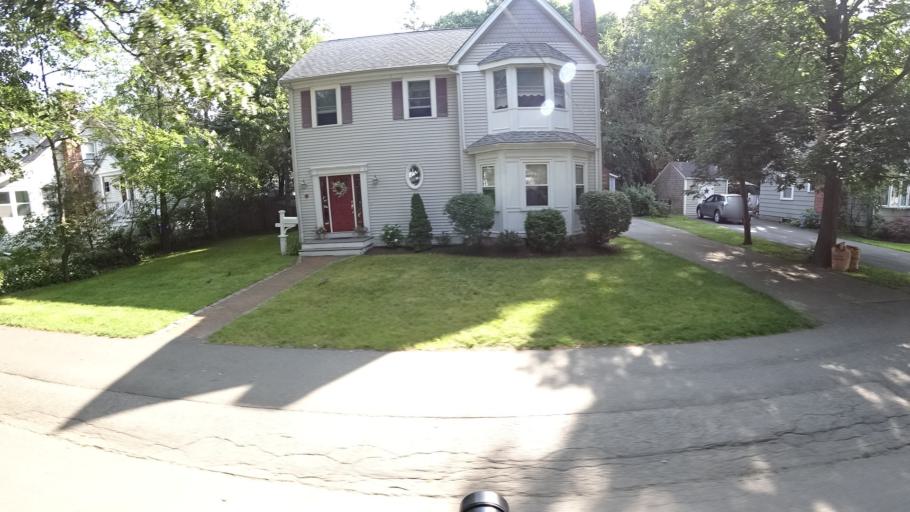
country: US
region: Massachusetts
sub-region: Norfolk County
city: Dedham
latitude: 42.2340
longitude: -71.1591
